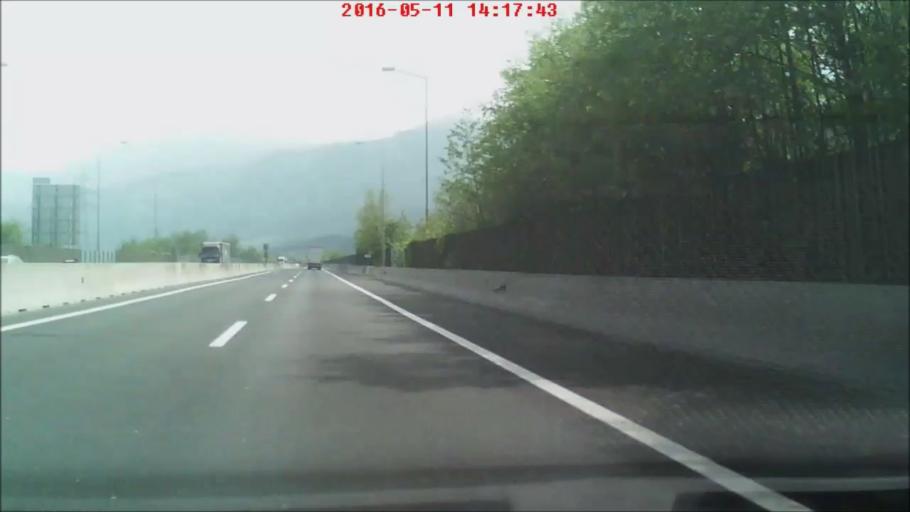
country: AT
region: Upper Austria
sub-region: Politischer Bezirk Kirchdorf an der Krems
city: Micheldorf in Oberoesterreich
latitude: 47.9195
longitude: 14.1017
